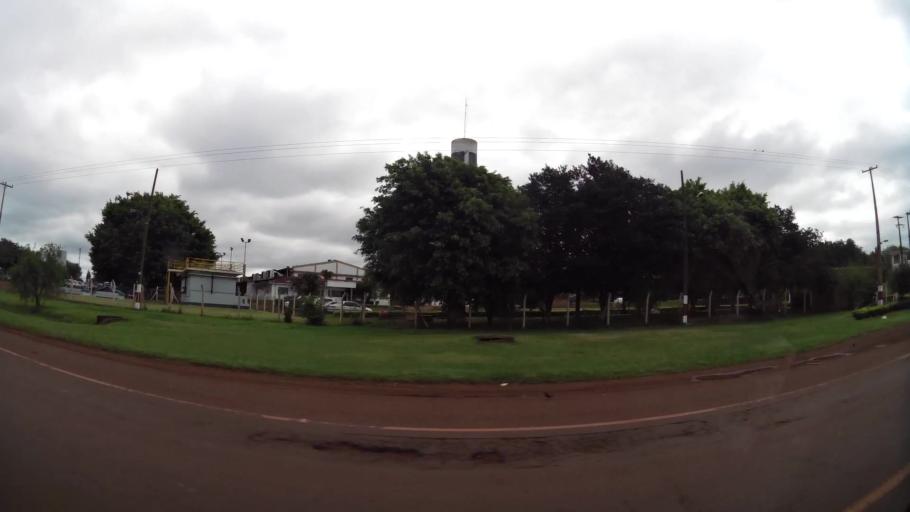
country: PY
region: Alto Parana
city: Ciudad del Este
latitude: -25.3814
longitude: -54.6431
